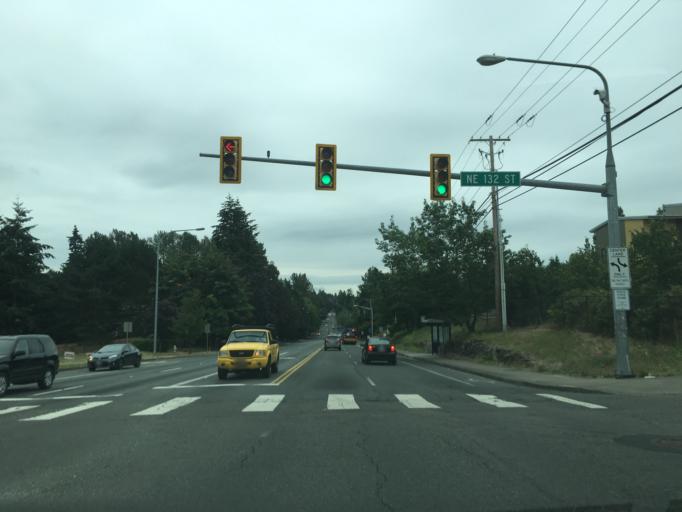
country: US
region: Washington
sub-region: King County
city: Inglewood-Finn Hill
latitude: 47.7185
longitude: -122.2078
